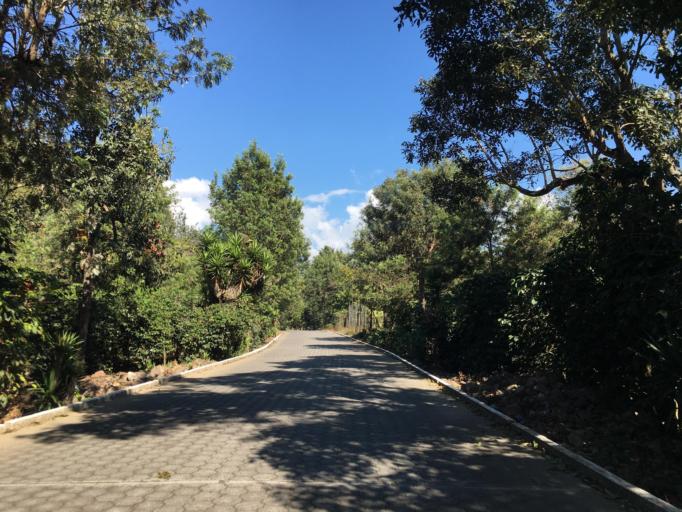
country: GT
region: Solola
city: Santiago Atitlan
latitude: 14.6610
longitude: -91.1765
